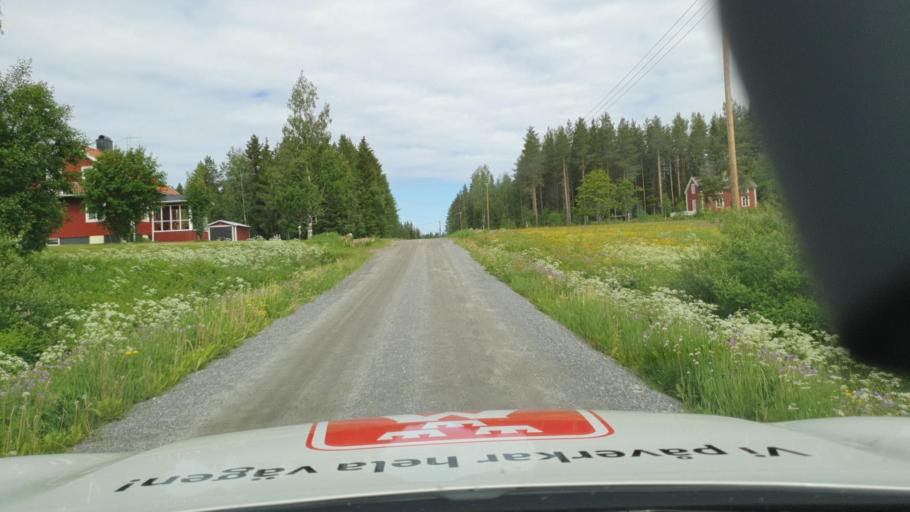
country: SE
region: Vaesterbotten
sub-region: Skelleftea Kommun
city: Langsele
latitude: 64.5739
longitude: 20.2982
